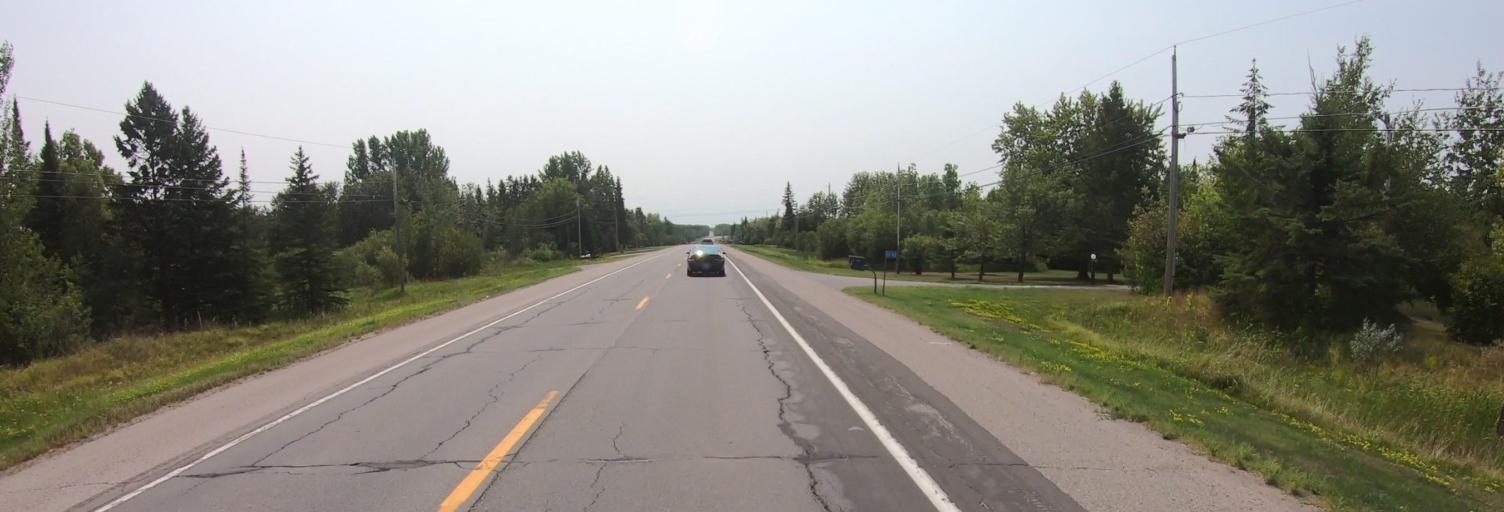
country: US
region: Minnesota
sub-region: Koochiching County
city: International Falls
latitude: 48.5669
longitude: -93.4401
